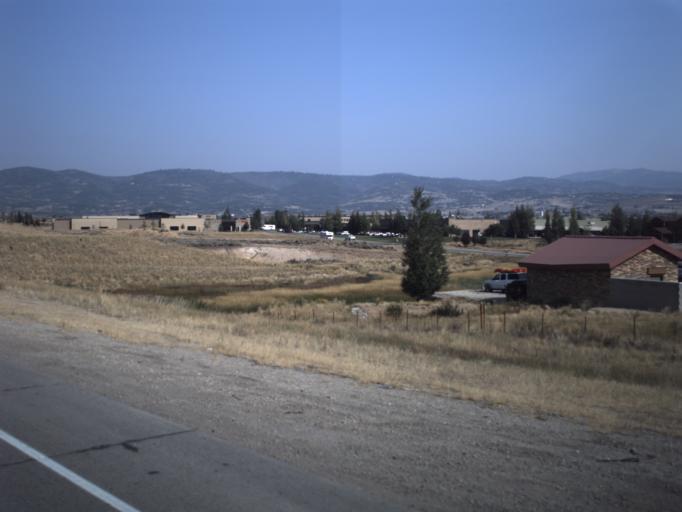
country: US
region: Utah
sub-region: Summit County
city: Snyderville
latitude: 40.7194
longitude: -111.4866
